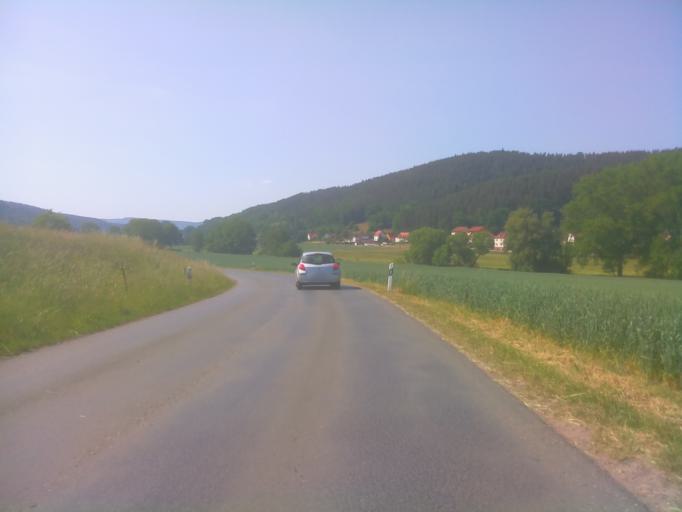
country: DE
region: Thuringia
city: Langenorla
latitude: 50.7364
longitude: 11.5903
